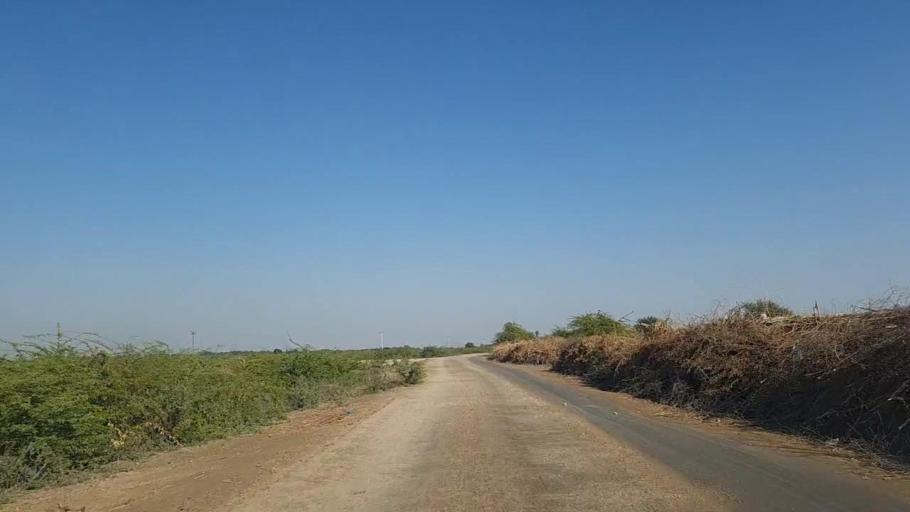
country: PK
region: Sindh
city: Naukot
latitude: 24.9457
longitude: 69.3413
